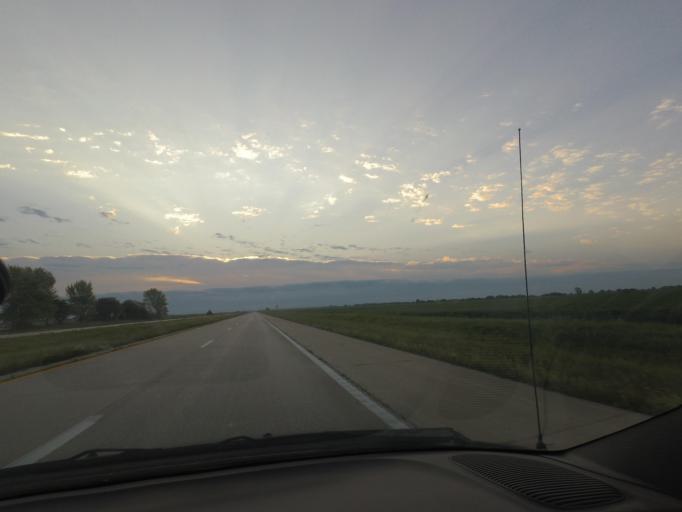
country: US
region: Missouri
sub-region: Macon County
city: Macon
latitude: 39.7501
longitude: -92.3308
